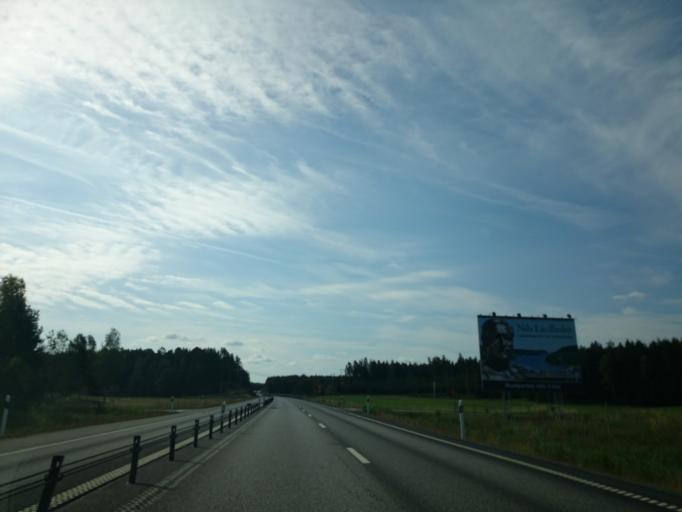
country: SE
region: OEstergoetland
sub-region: Valdemarsviks Kommun
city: Gusum
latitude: 58.2456
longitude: 16.5379
